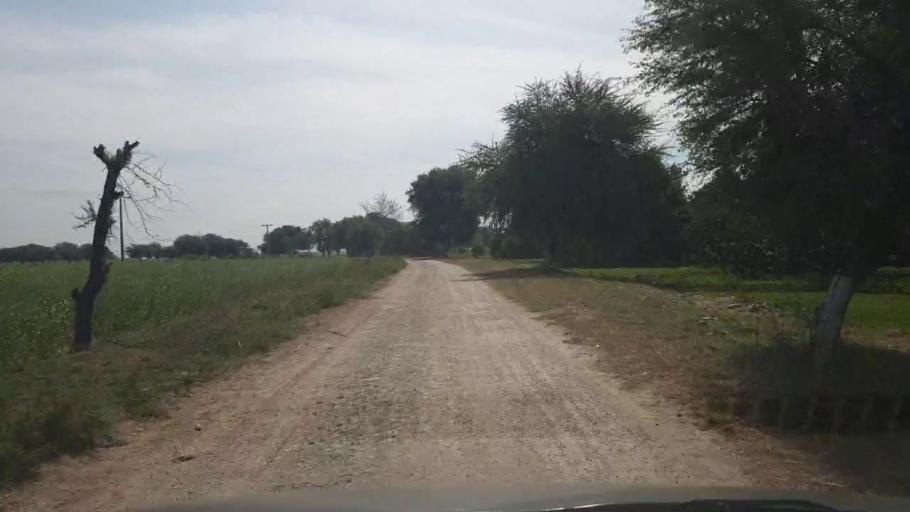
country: PK
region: Sindh
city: Umarkot
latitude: 25.3406
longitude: 69.5935
